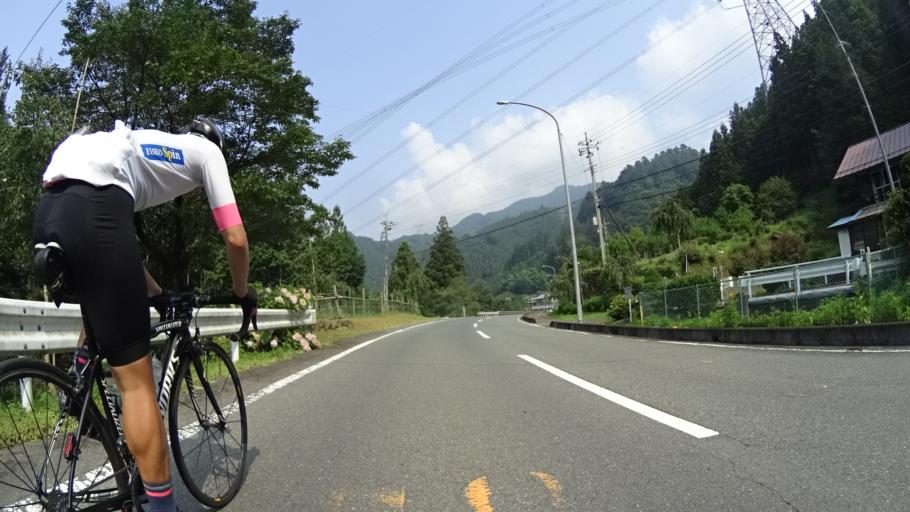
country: JP
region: Saitama
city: Chichibu
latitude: 36.0320
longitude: 138.9380
